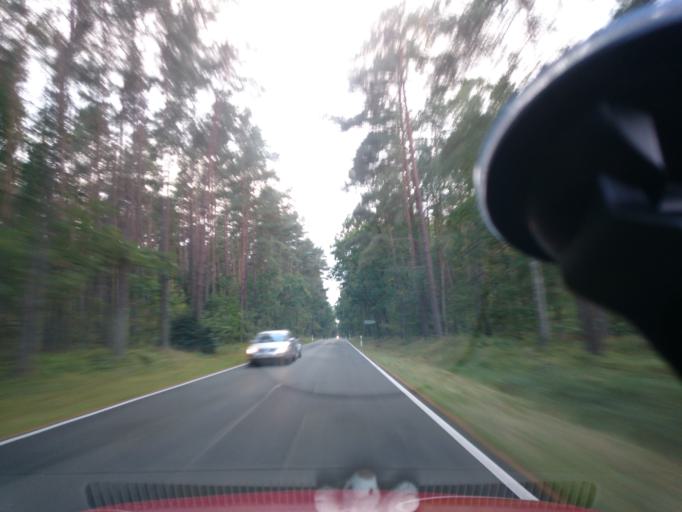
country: DE
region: Mecklenburg-Vorpommern
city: Born
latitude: 54.3440
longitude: 12.5791
